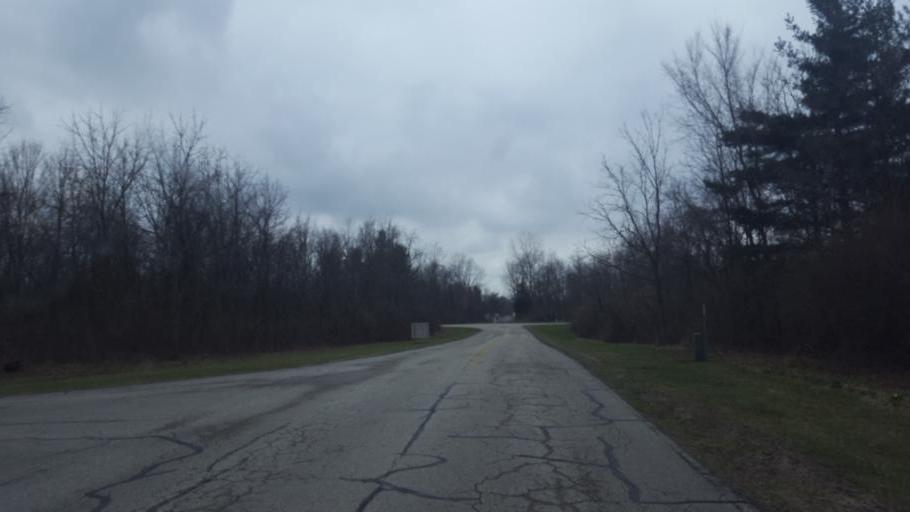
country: US
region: Ohio
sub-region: Delaware County
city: Delaware
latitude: 40.3788
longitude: -83.0631
